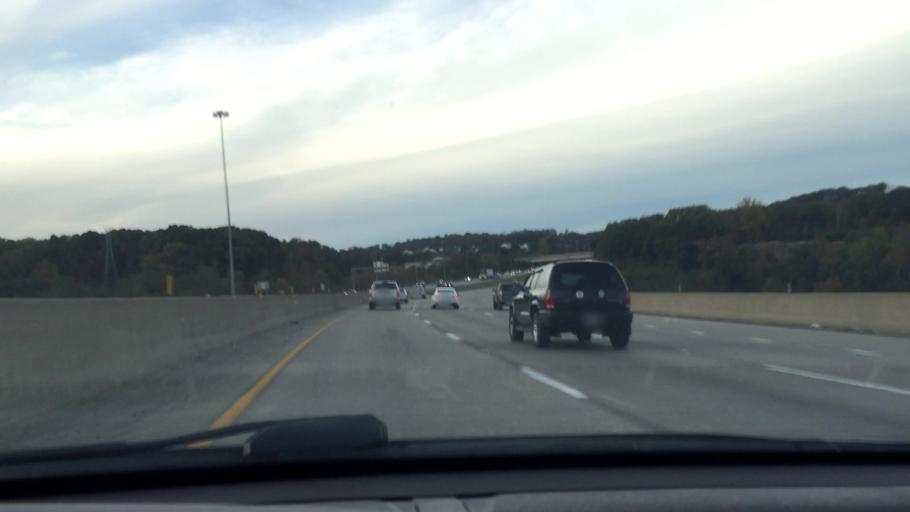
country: US
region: Pennsylvania
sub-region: Allegheny County
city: Heidelberg
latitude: 40.3993
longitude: -80.1054
